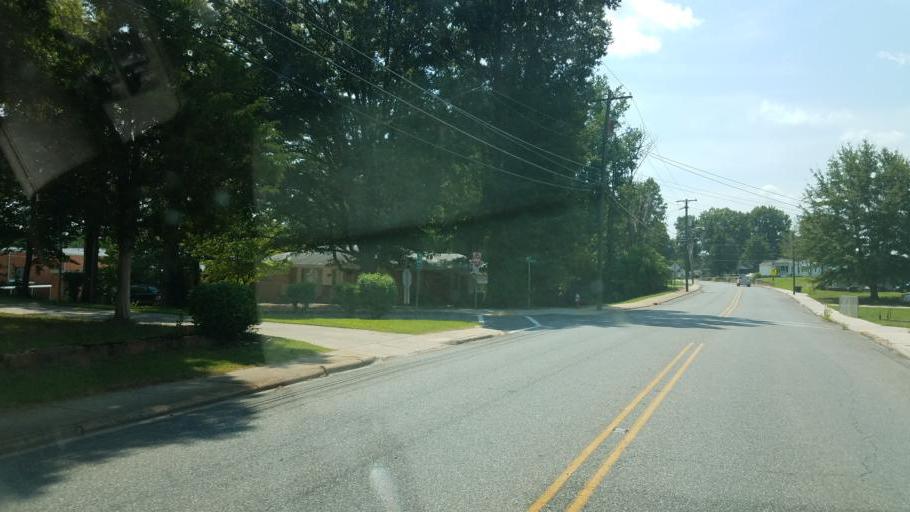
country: US
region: North Carolina
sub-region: Gaston County
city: Cherryville
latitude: 35.3725
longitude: -81.3773
